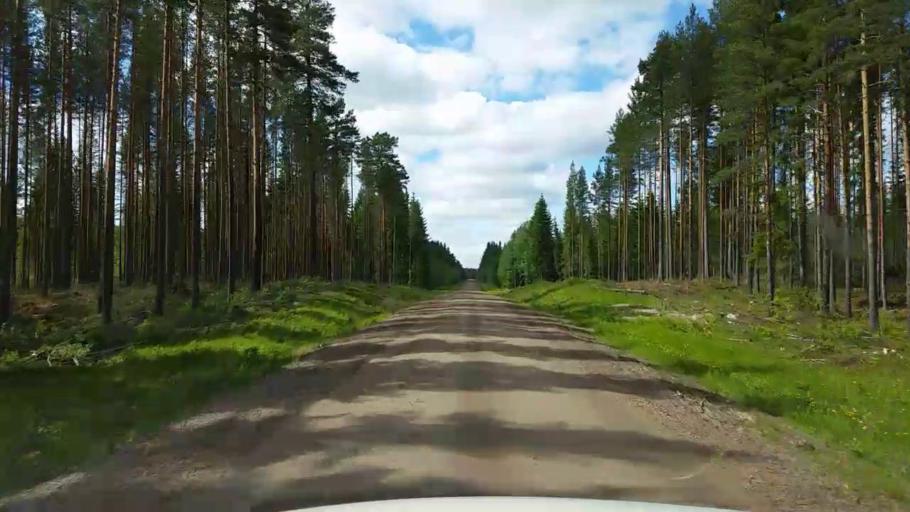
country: SE
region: Gaevleborg
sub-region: Ovanakers Kommun
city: Alfta
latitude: 61.4723
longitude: 16.0160
